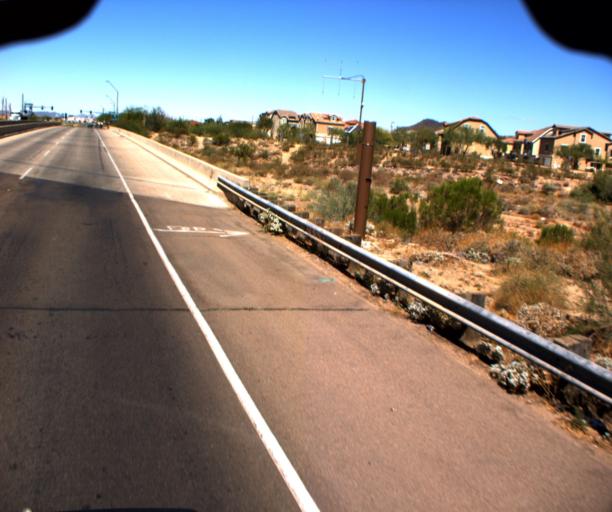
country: US
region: Arizona
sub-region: Maricopa County
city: Anthem
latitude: 33.7984
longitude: -112.1229
